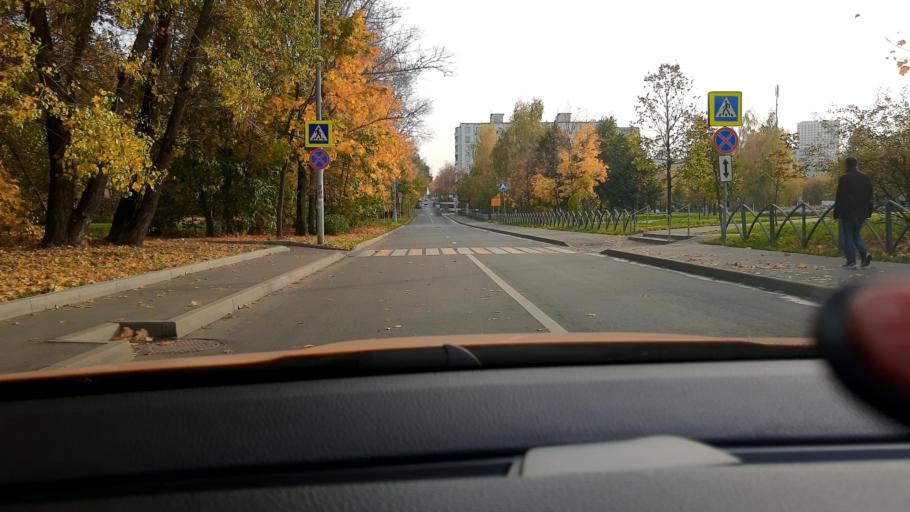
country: RU
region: Moscow
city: Vagonoremont
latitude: 55.8953
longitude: 37.5366
